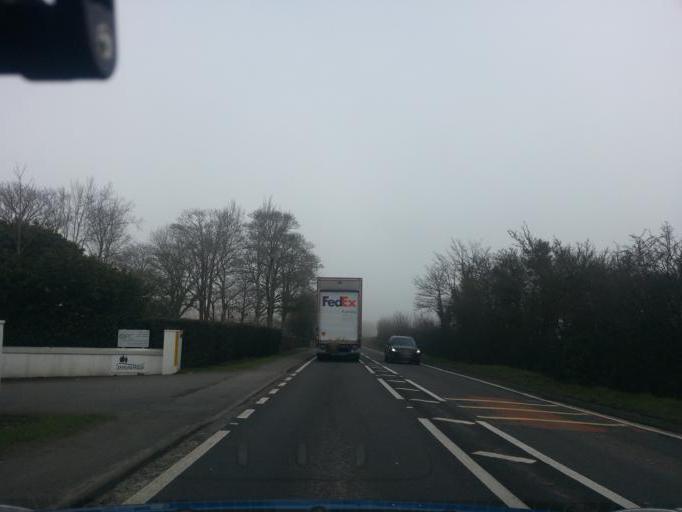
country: GB
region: England
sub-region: Oxfordshire
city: Boars Hill
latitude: 51.7219
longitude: -1.3316
